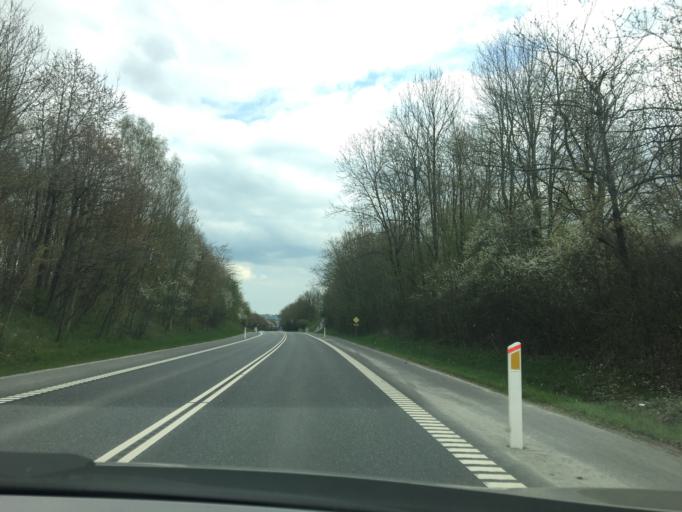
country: DK
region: Central Jutland
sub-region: Horsens Kommune
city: Braedstrup
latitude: 55.9533
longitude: 9.6273
